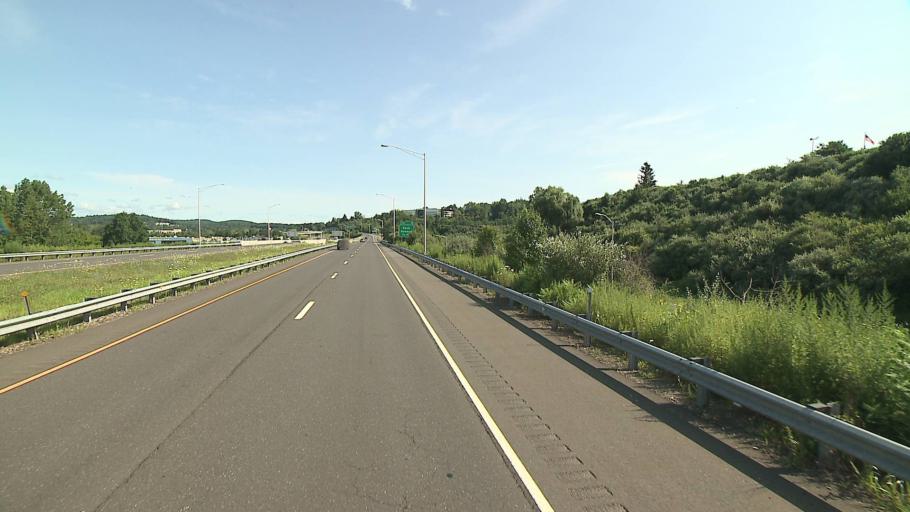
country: US
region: Connecticut
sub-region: Fairfield County
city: Danbury
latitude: 41.3700
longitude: -73.4739
